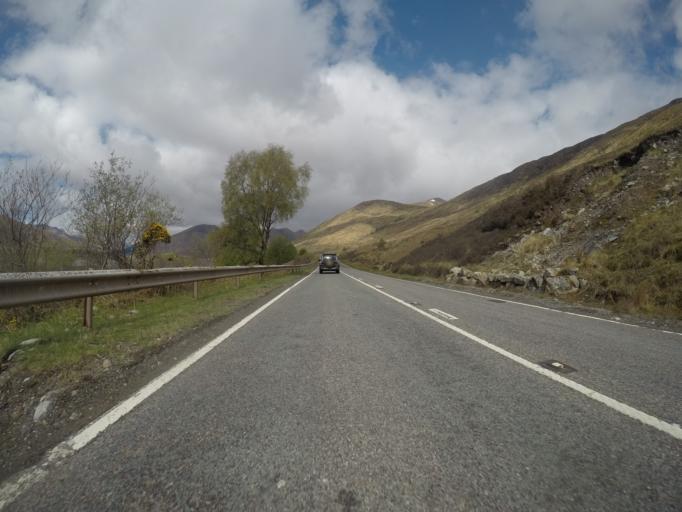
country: GB
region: Scotland
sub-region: Highland
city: Spean Bridge
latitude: 57.1499
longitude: -5.1210
